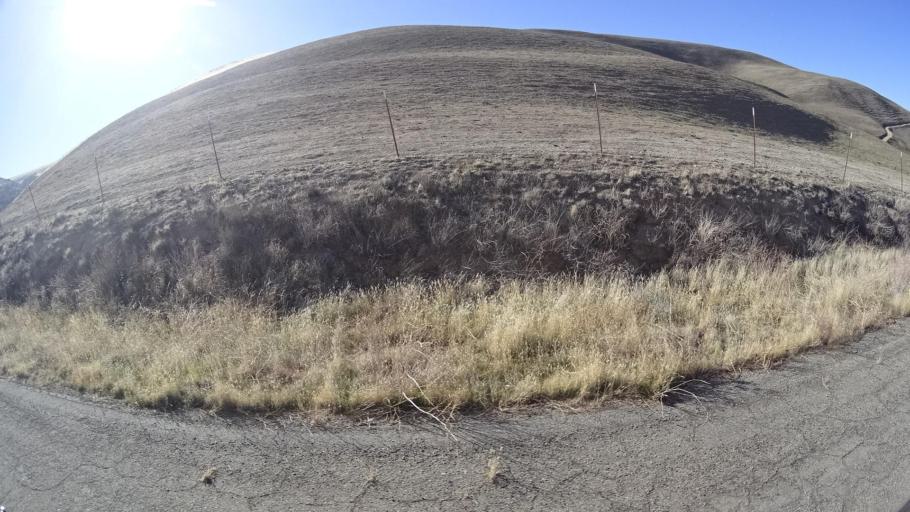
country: US
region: California
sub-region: Kern County
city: Maricopa
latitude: 34.9543
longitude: -119.4066
